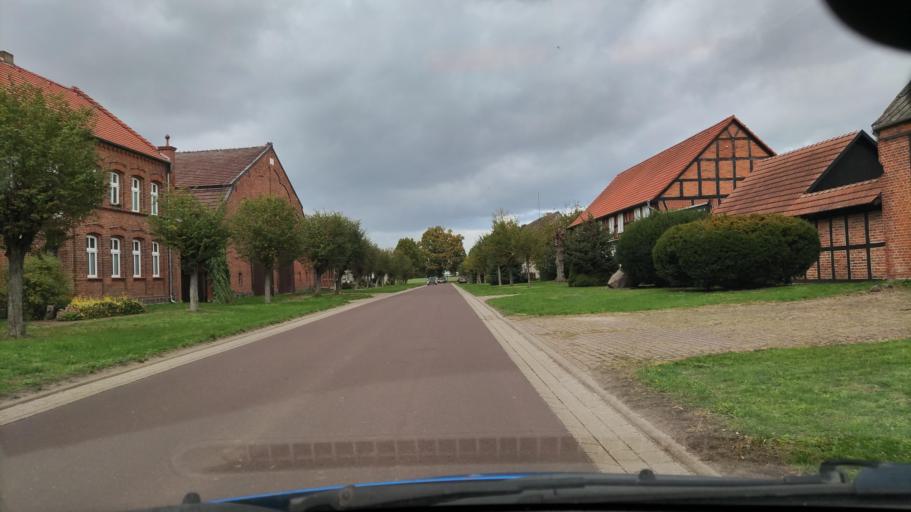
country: DE
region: Saxony-Anhalt
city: Luftkurort Arendsee
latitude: 52.8307
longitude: 11.3939
